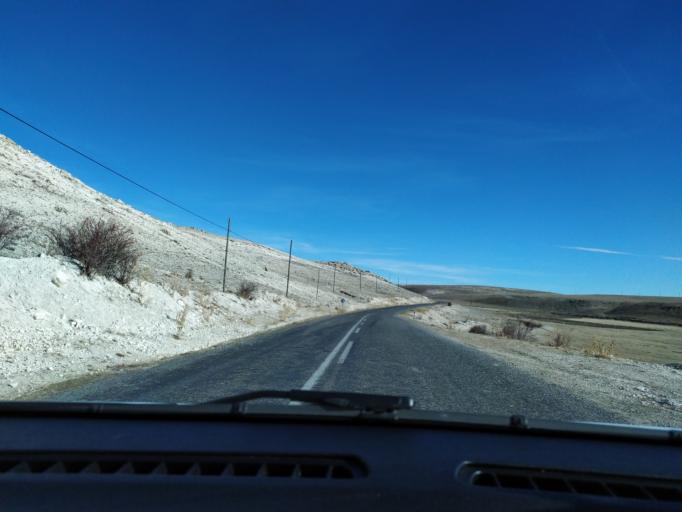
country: TR
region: Kayseri
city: Orensehir
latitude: 38.9784
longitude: 36.6663
